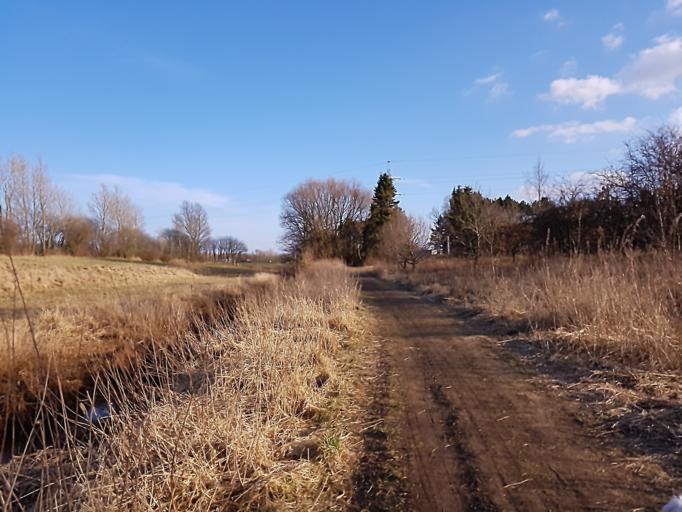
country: DK
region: South Denmark
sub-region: Esbjerg Kommune
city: Bramming
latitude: 55.4822
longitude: 8.6985
